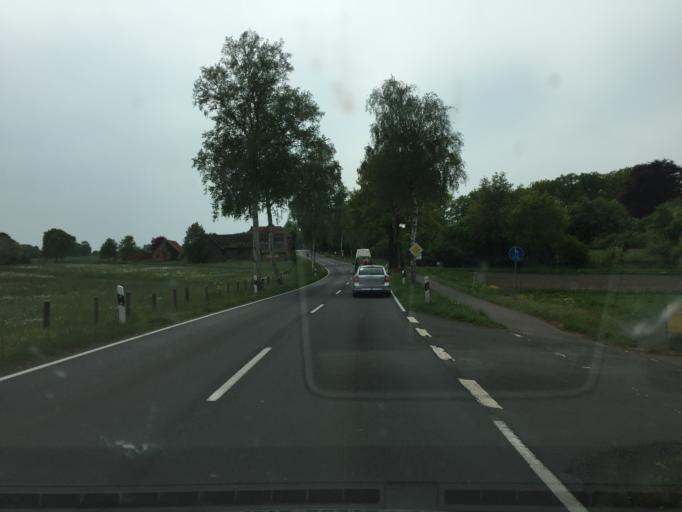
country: DE
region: Lower Saxony
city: Syke
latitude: 52.8837
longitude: 8.7811
